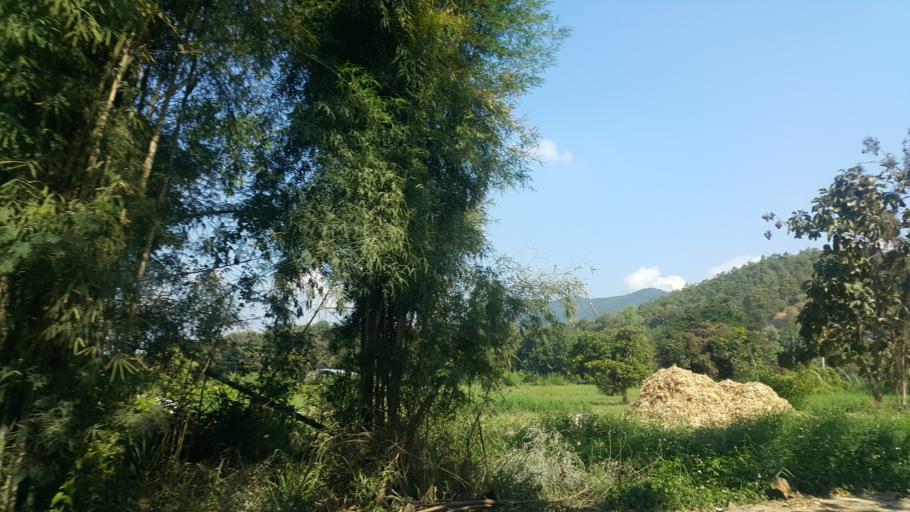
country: TH
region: Lamphun
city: Ban Thi
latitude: 18.6786
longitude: 99.1701
